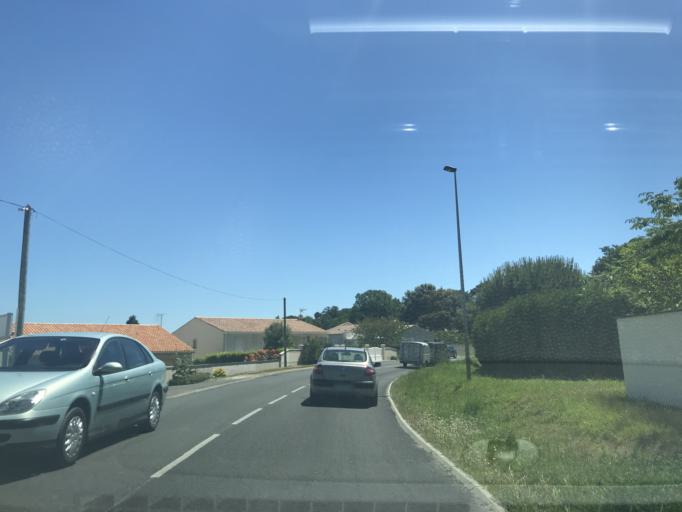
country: FR
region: Poitou-Charentes
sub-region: Departement de la Charente-Maritime
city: Meschers-sur-Gironde
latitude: 45.5704
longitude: -0.9606
